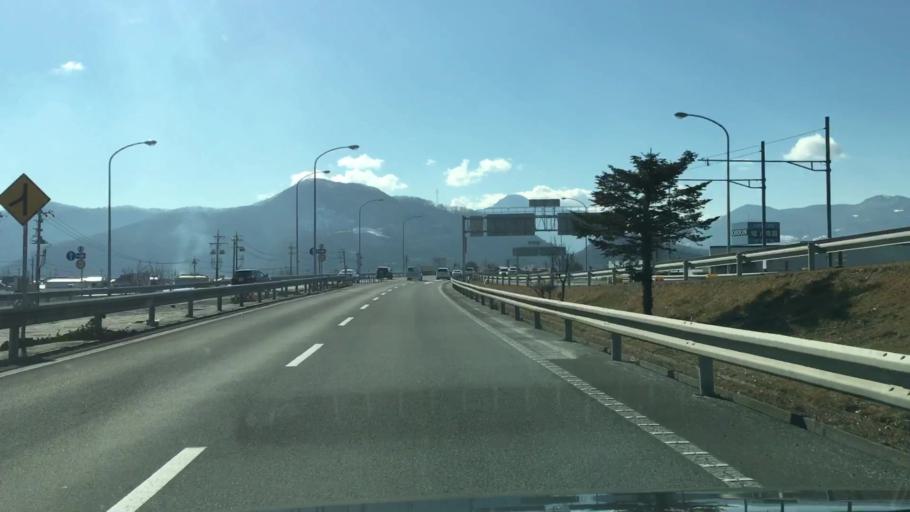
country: JP
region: Nagano
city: Nagano-shi
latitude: 36.5510
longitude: 138.1413
